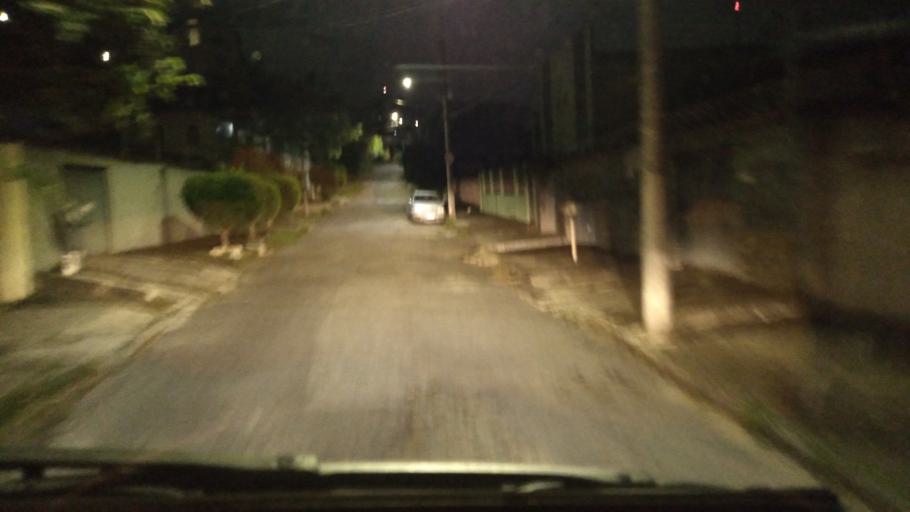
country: BR
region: Minas Gerais
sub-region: Belo Horizonte
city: Belo Horizonte
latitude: -19.8966
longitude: -43.9744
